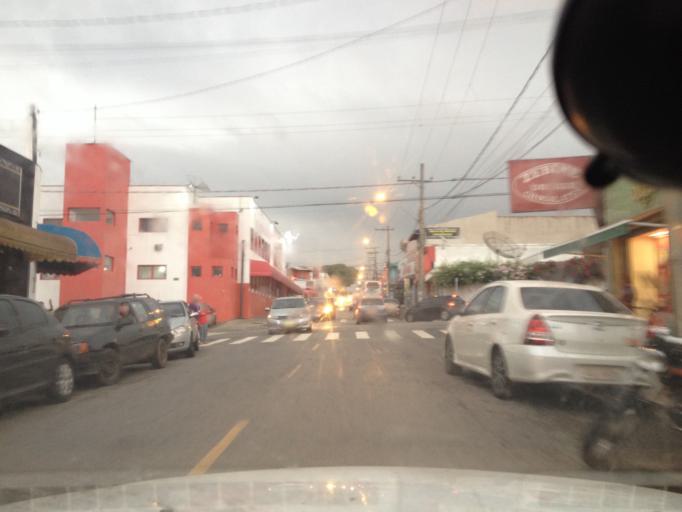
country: BR
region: Sao Paulo
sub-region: Salto
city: Salto
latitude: -23.1930
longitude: -47.2733
